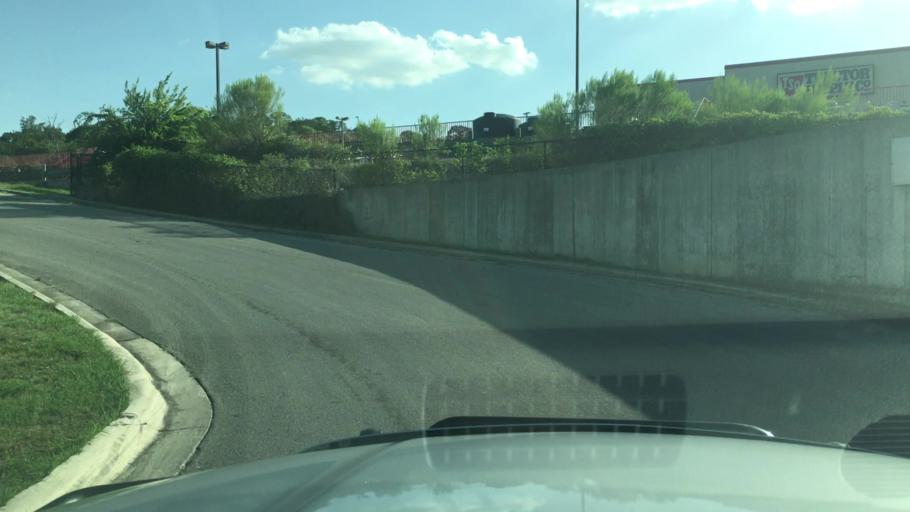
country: US
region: Texas
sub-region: Comal County
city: Bulverde
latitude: 29.7963
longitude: -98.4203
